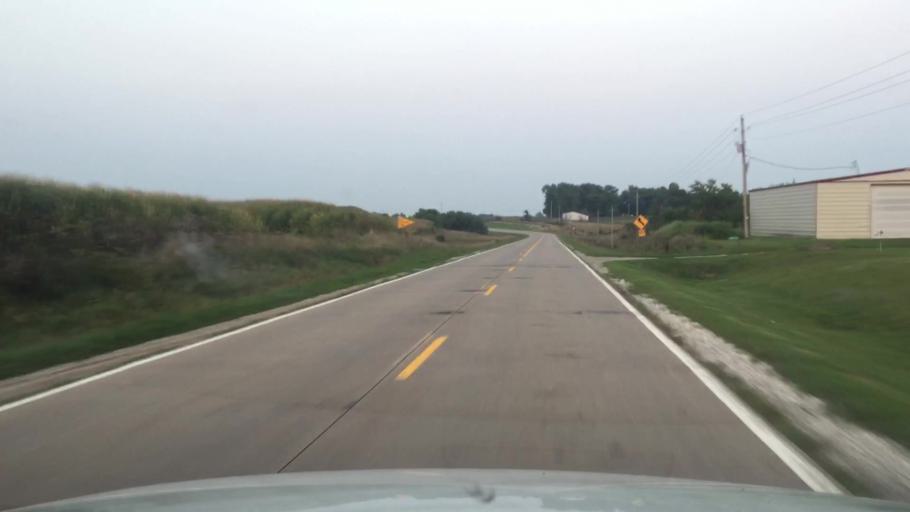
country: US
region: Iowa
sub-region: Clarke County
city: Osceola
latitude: 41.1875
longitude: -93.6799
